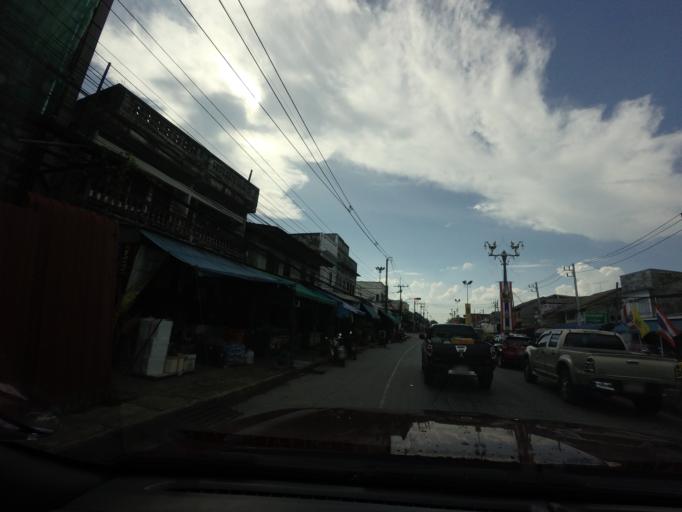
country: TH
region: Pattani
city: Khok Pho
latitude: 6.6783
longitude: 101.1462
